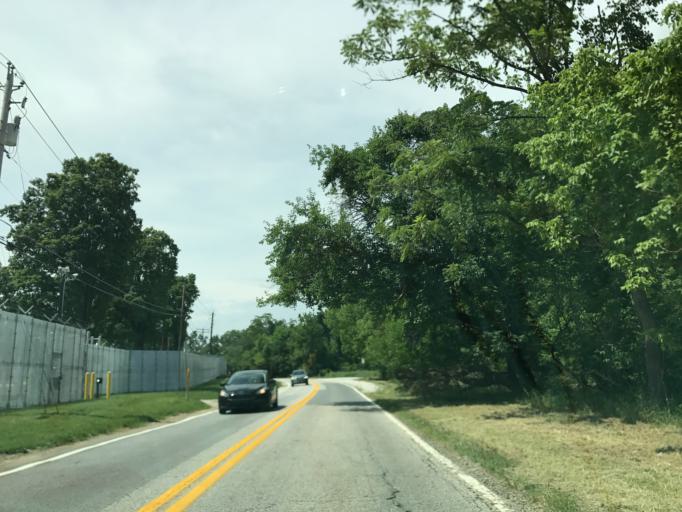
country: US
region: Maryland
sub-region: Baltimore County
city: Cockeysville
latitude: 39.4934
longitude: -76.6805
